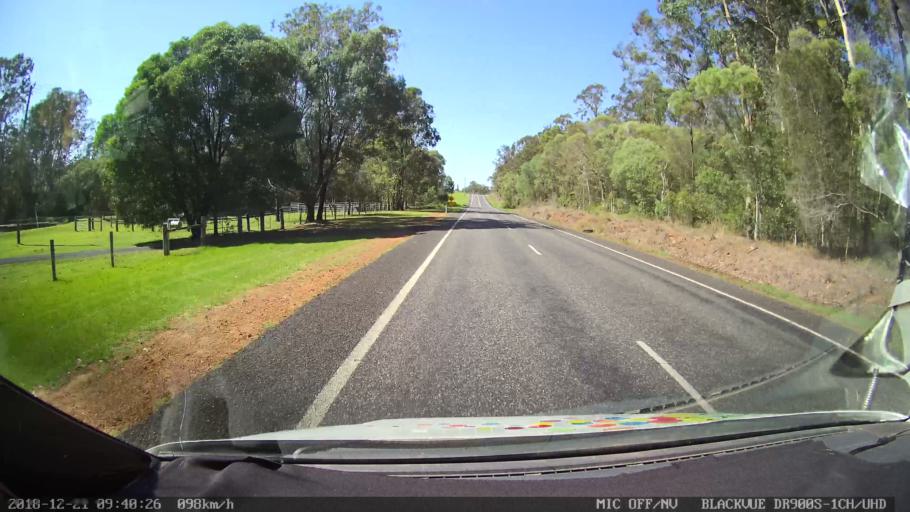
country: AU
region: New South Wales
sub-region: Clarence Valley
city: Grafton
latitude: -29.5724
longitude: 152.9635
